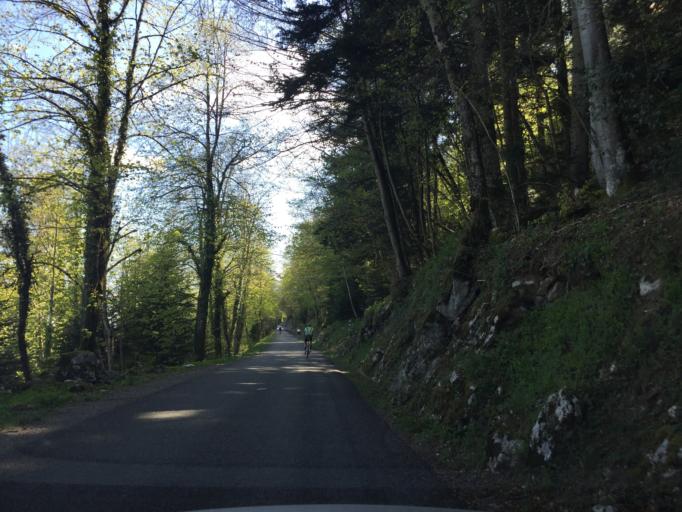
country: FR
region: Rhone-Alpes
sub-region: Departement de la Savoie
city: La Motte-Servolex
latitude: 45.5864
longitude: 5.8261
